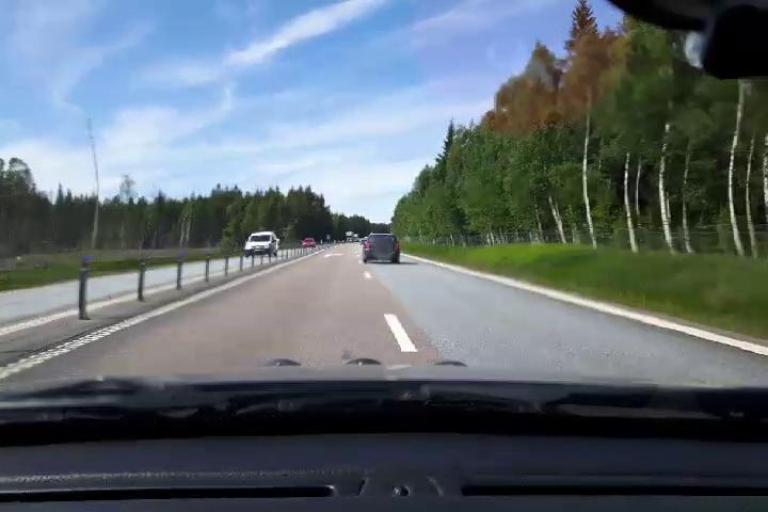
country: SE
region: Gaevleborg
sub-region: Gavle Kommun
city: Norrsundet
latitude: 60.8688
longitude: 17.0544
